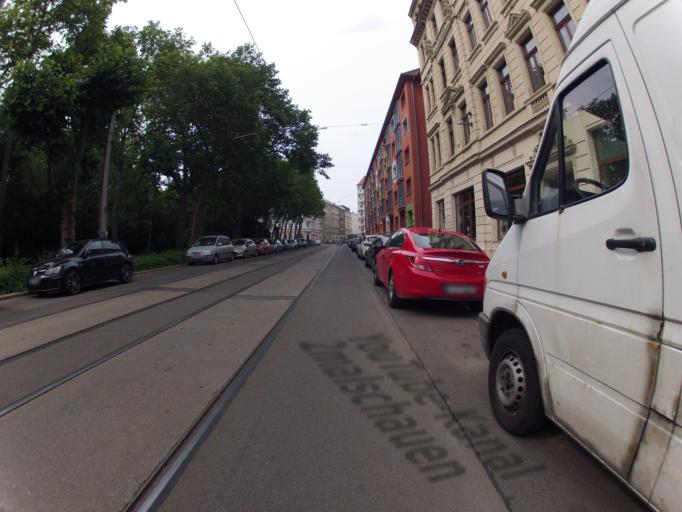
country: DE
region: Saxony
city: Leipzig
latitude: 51.3232
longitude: 12.3786
